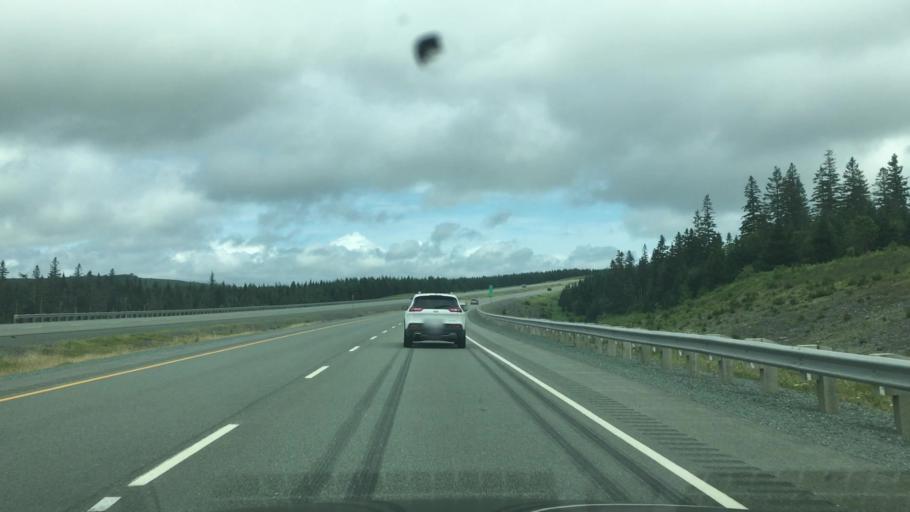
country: CA
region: Nova Scotia
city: Oxford
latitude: 45.5497
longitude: -63.7130
